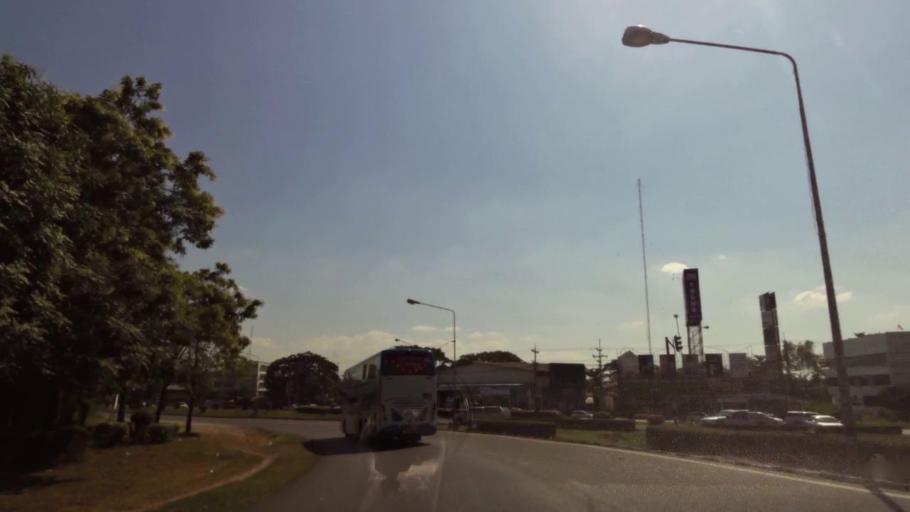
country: TH
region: Nakhon Sawan
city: Nakhon Sawan
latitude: 15.7064
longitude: 100.1116
